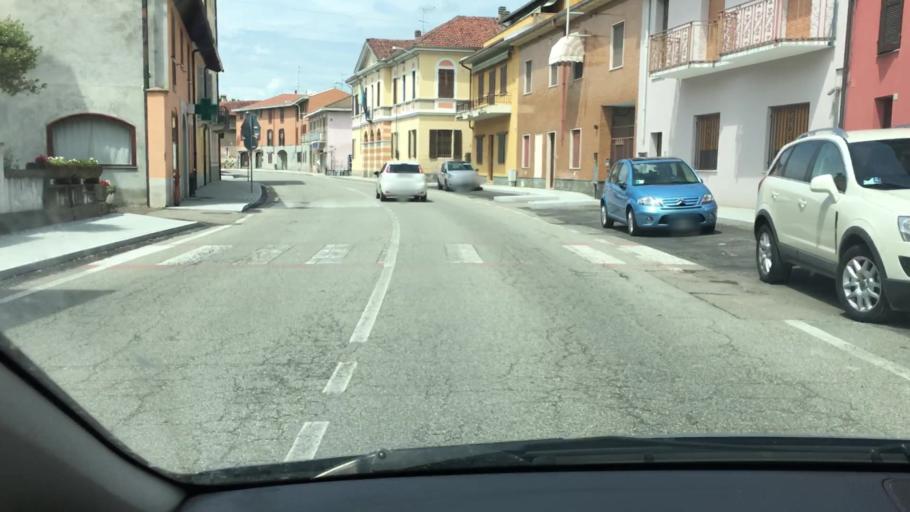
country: IT
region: Piedmont
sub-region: Provincia di Novara
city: Casalbeltrame
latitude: 45.4356
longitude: 8.4684
